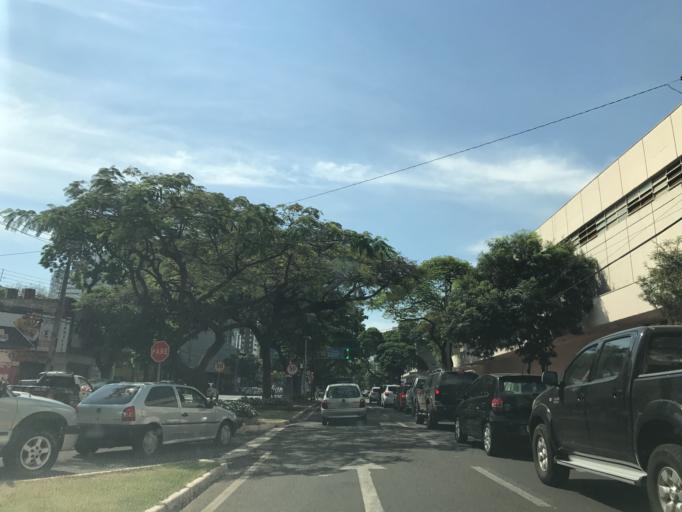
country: BR
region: Parana
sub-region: Maringa
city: Maringa
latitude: -23.4218
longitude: -51.9330
